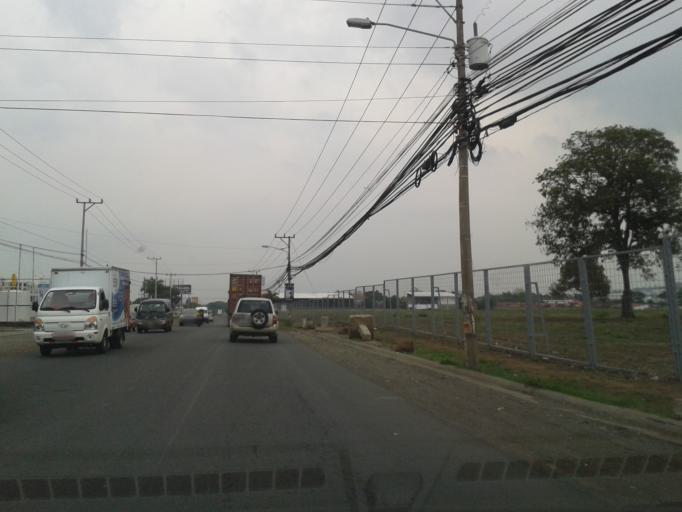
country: CR
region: Heredia
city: San Francisco
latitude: 9.9681
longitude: -84.1240
